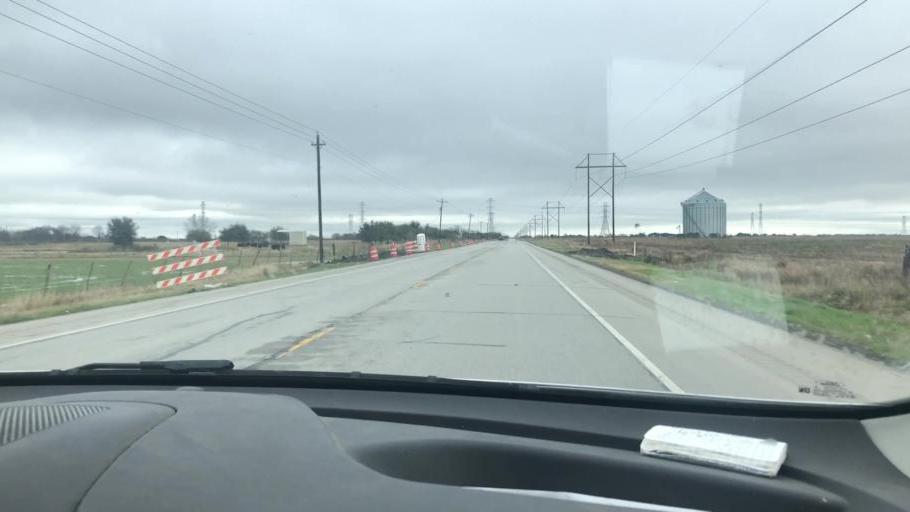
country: US
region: Texas
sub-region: Wharton County
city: Boling
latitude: 29.1798
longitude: -96.0078
